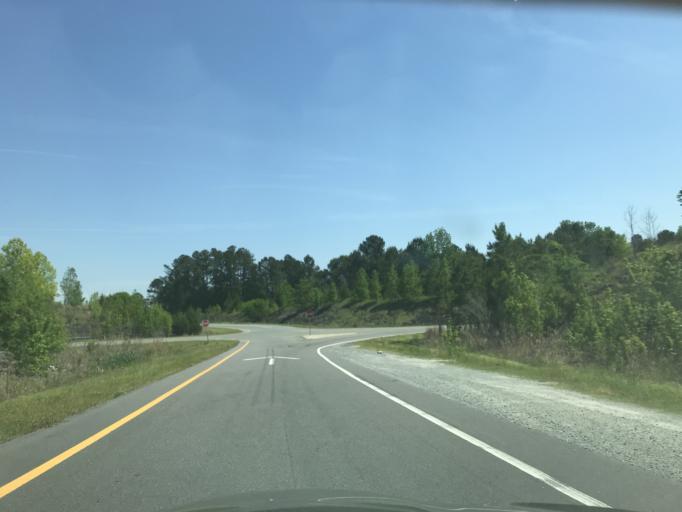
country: US
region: North Carolina
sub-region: Johnston County
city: Benson
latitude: 35.3294
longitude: -78.4502
